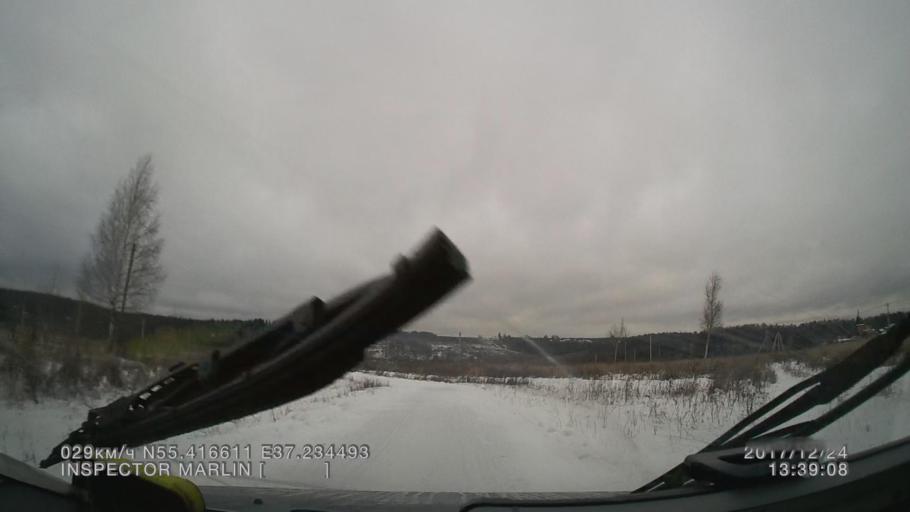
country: RU
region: Moskovskaya
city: Troitsk
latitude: 55.4158
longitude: 37.2346
